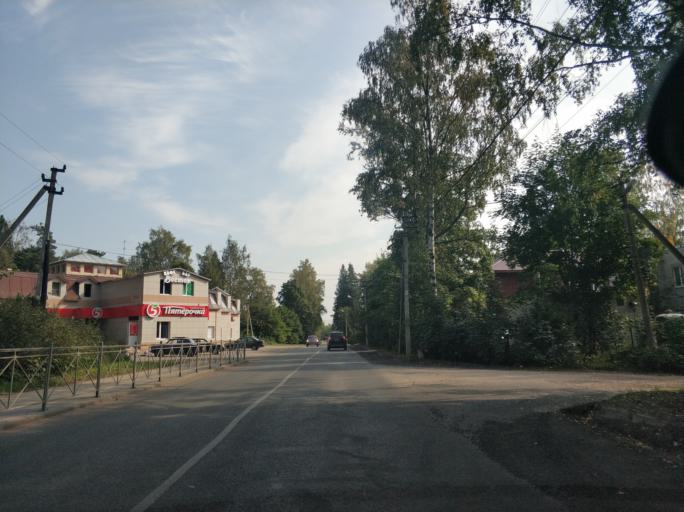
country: RU
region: Leningrad
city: Vsevolozhsk
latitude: 60.0199
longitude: 30.6687
